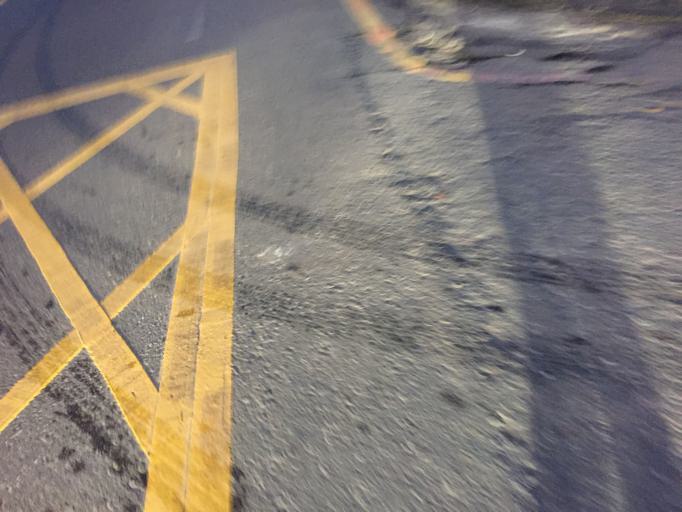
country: TW
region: Taiwan
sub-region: Yilan
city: Yilan
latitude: 24.6601
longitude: 121.7786
